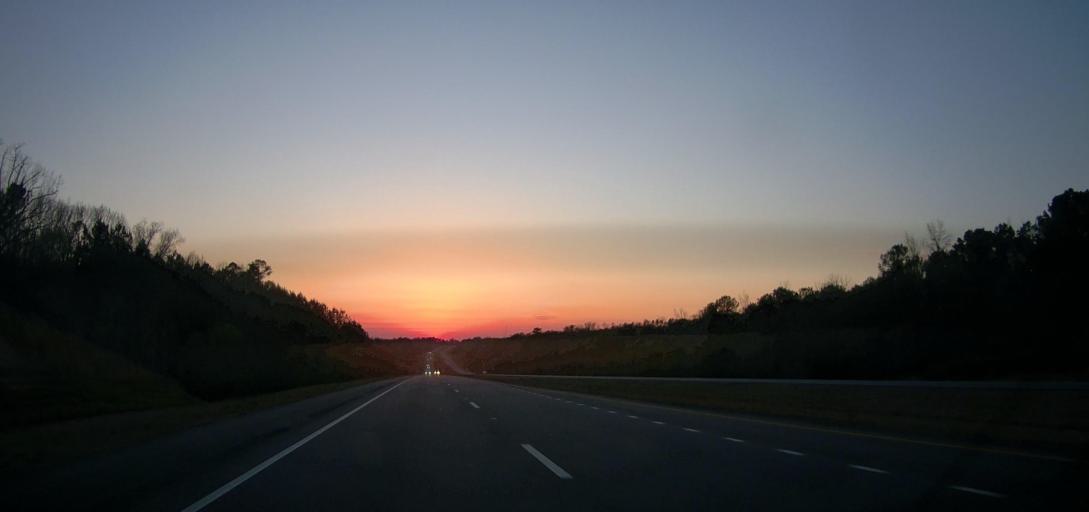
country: US
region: Alabama
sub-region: Tallapoosa County
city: Dadeville
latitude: 32.8794
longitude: -85.8258
